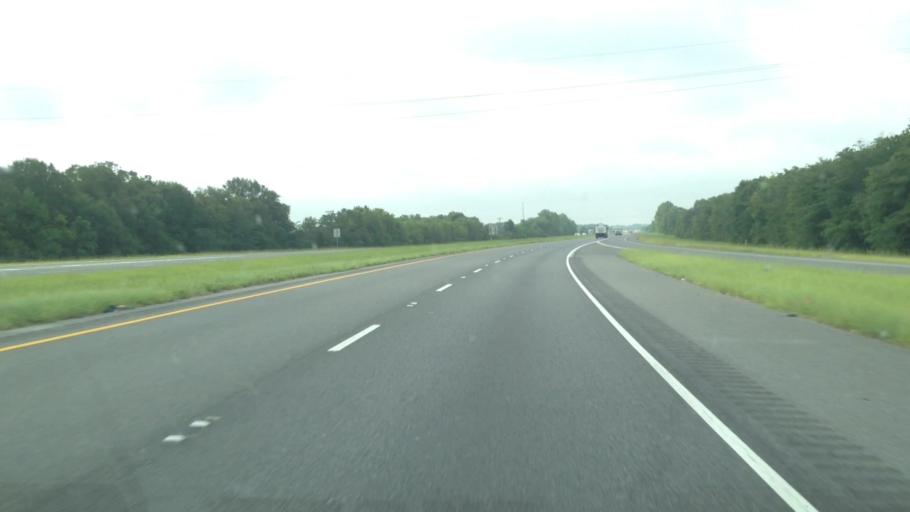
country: US
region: Louisiana
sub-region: Saint Landry Parish
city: Opelousas
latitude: 30.6387
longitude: -92.0485
